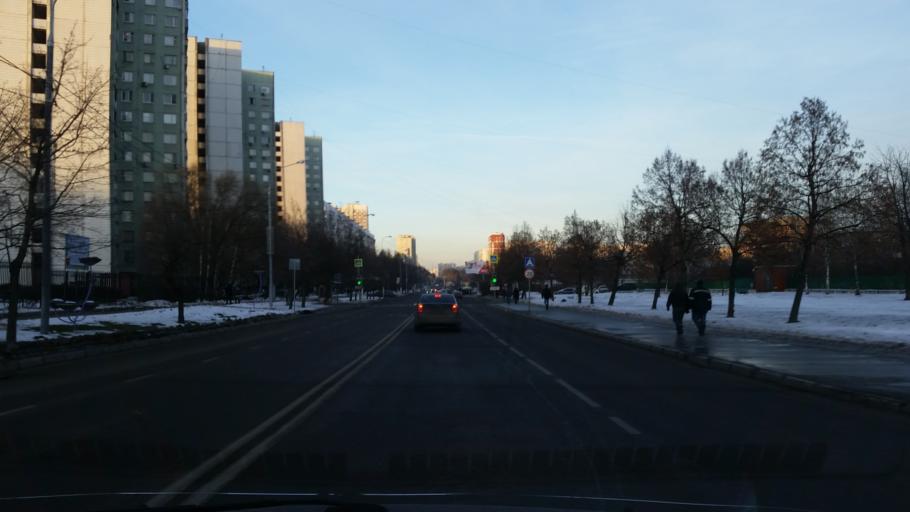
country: RU
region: Moscow
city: Chertanovo Yuzhnoye
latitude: 55.6159
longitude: 37.6057
